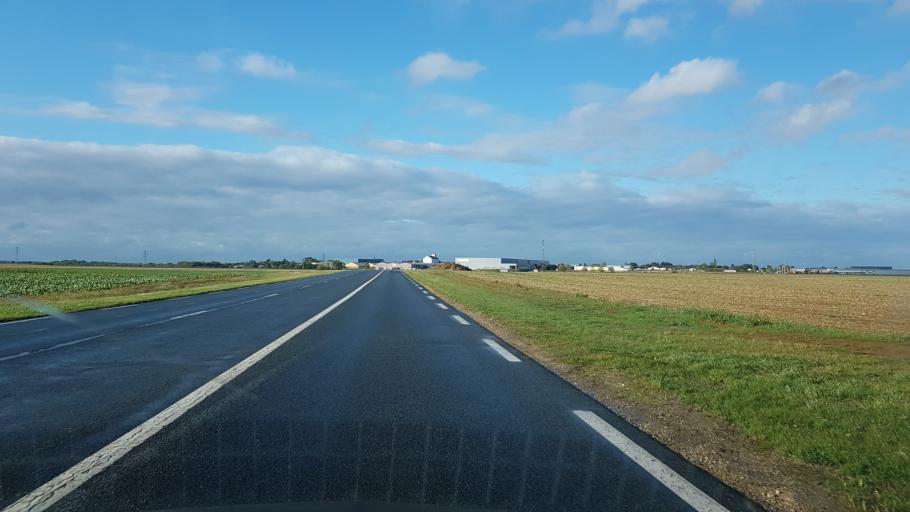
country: FR
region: Centre
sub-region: Departement du Loiret
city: Sermaises
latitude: 48.2810
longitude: 2.2083
